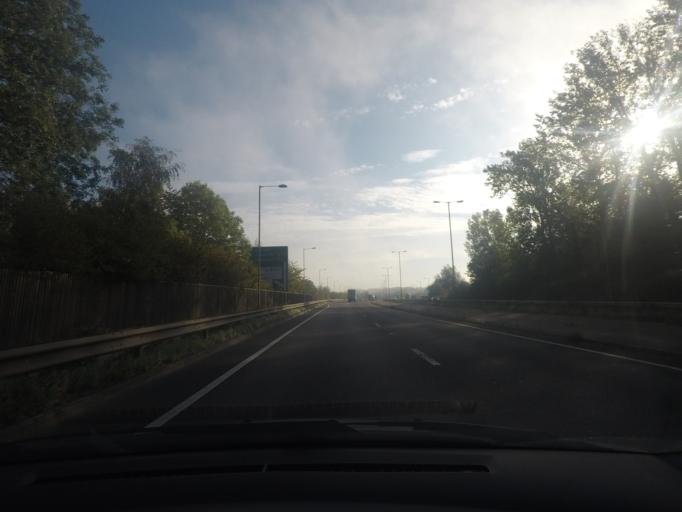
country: GB
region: England
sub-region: East Riding of Yorkshire
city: North Ferriby
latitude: 53.7254
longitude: -0.5285
